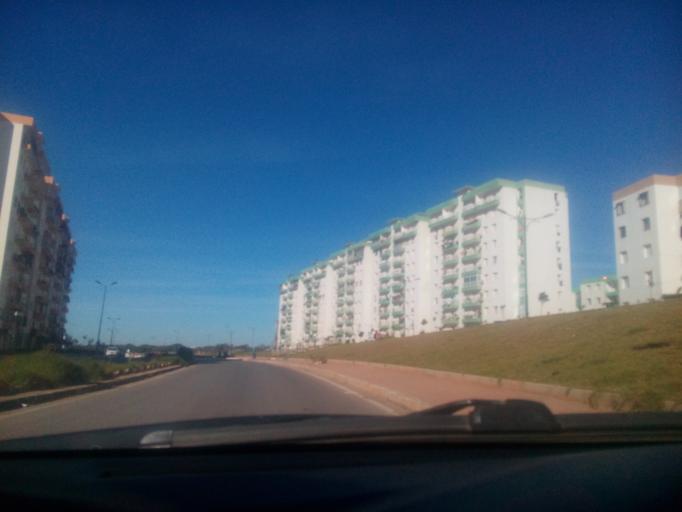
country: DZ
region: Oran
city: Bir el Djir
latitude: 35.7530
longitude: -0.5546
